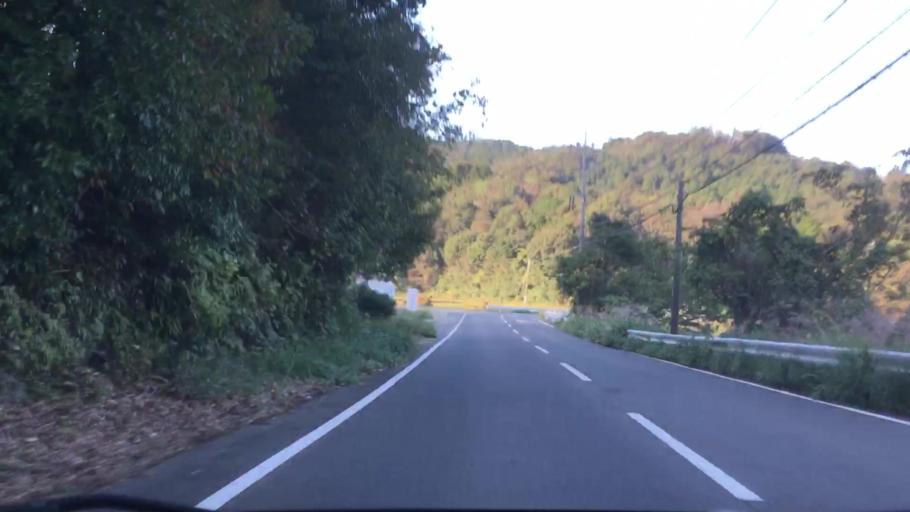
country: JP
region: Nagasaki
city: Sasebo
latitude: 32.9544
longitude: 129.6755
